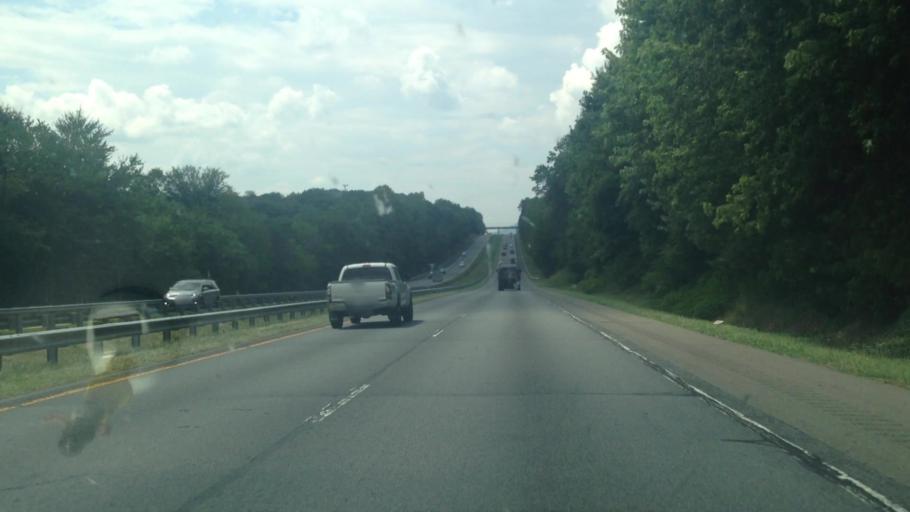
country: US
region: North Carolina
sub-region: Stokes County
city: King
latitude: 36.2782
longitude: -80.3840
